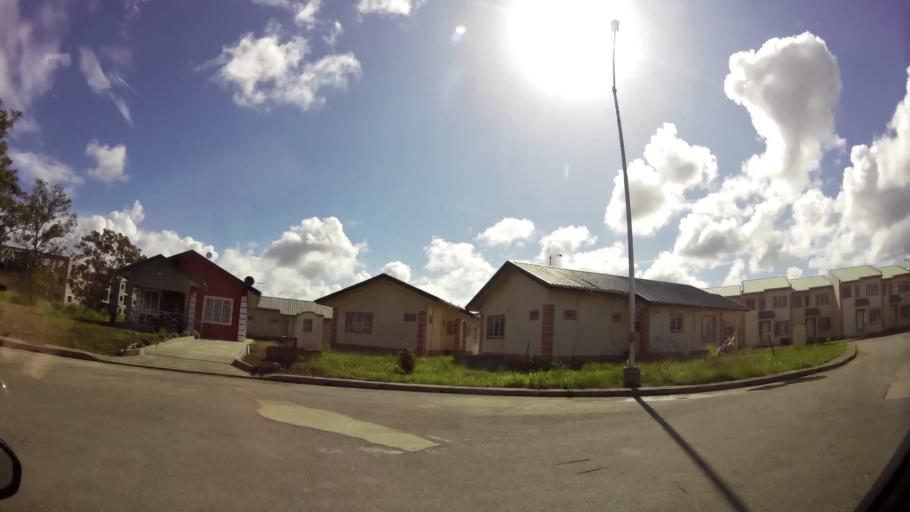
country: TT
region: Chaguanas
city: Chaguanas
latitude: 10.5355
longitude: -61.3929
